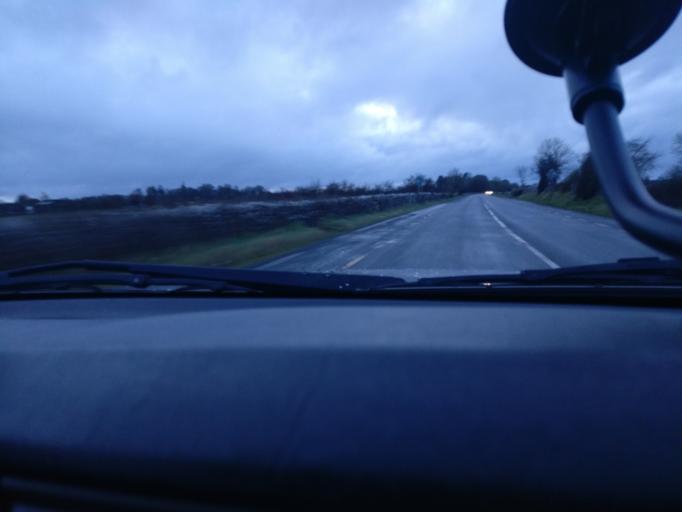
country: IE
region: Connaught
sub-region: County Galway
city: Loughrea
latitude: 53.2227
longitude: -8.4603
